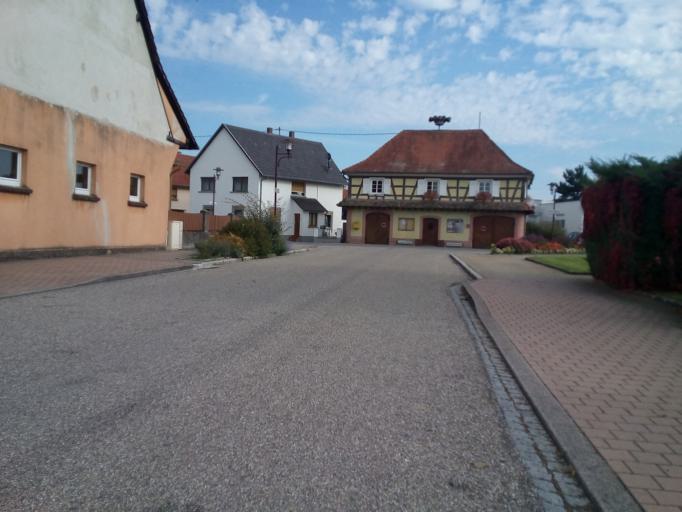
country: FR
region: Alsace
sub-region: Departement du Bas-Rhin
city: Herrlisheim
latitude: 48.7112
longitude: 7.9120
